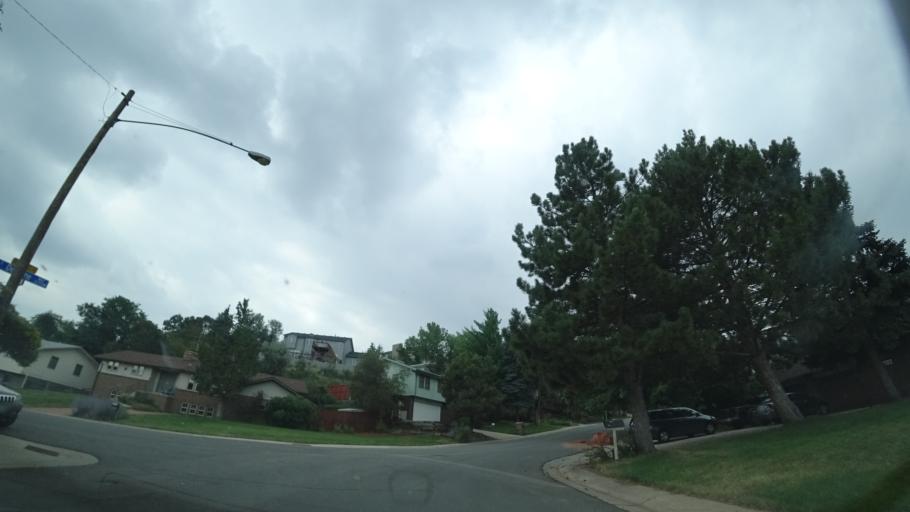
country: US
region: Colorado
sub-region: Jefferson County
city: West Pleasant View
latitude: 39.7015
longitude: -105.1544
